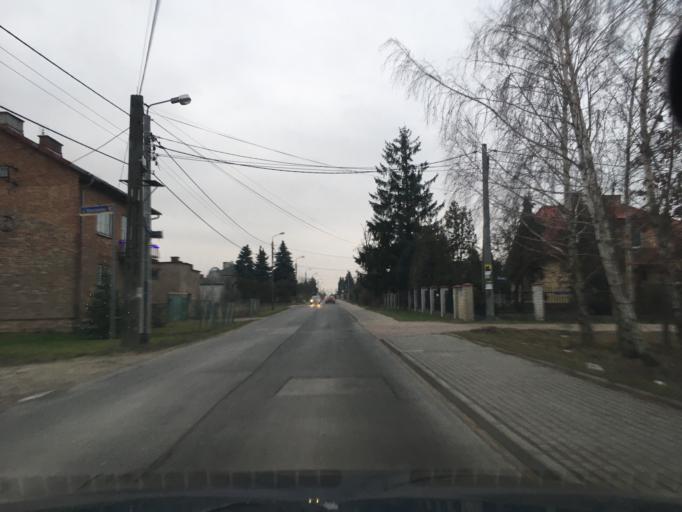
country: PL
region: Masovian Voivodeship
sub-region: Powiat piaseczynski
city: Mysiadlo
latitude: 52.1236
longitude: 20.9795
